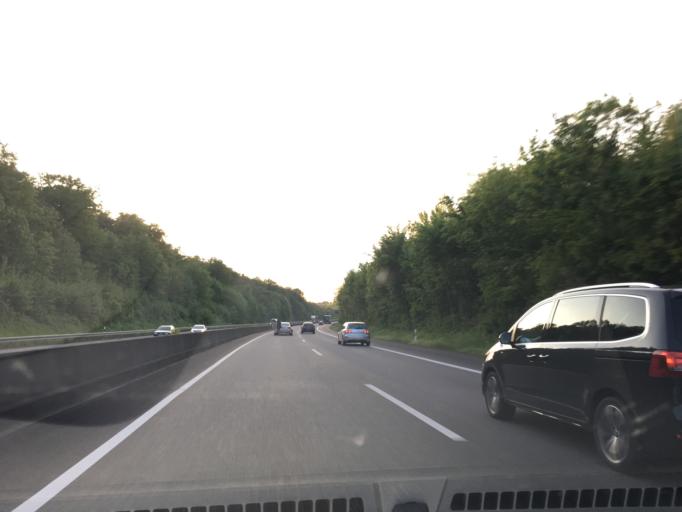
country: DE
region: Lower Saxony
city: Osnabrueck
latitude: 52.2478
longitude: 8.0247
